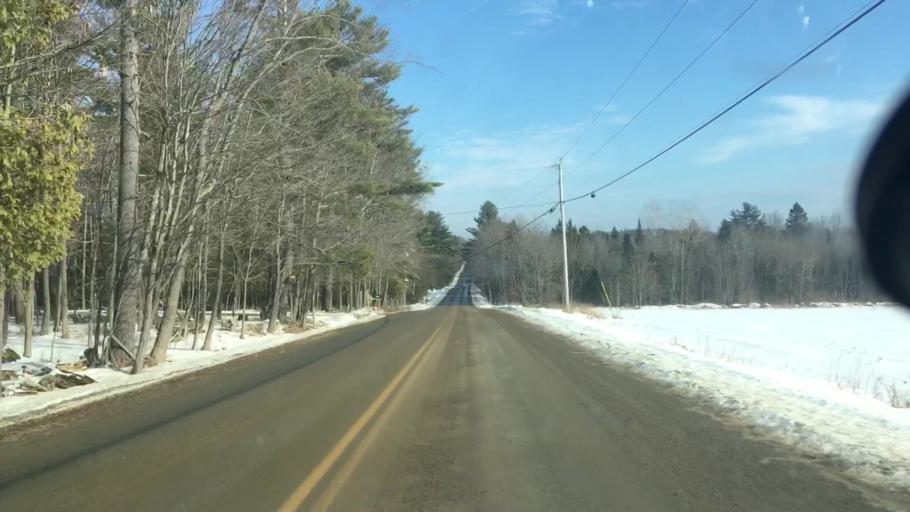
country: US
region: Maine
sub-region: Penobscot County
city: Levant
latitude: 44.8623
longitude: -68.8783
